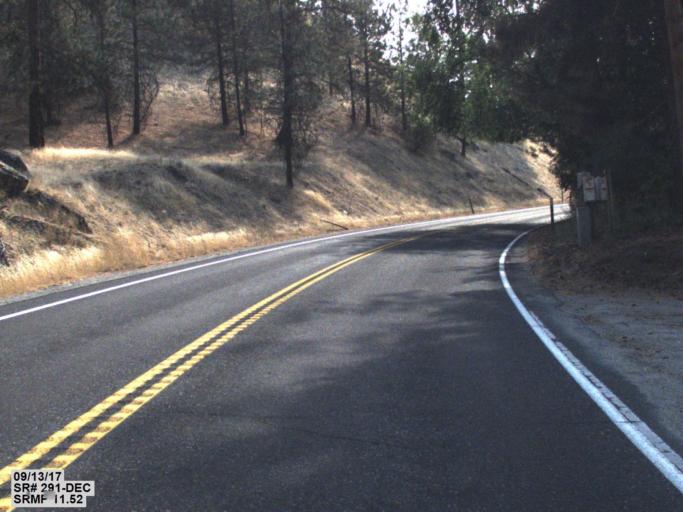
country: US
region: Washington
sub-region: Spokane County
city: Fairwood
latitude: 47.8000
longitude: -117.5403
